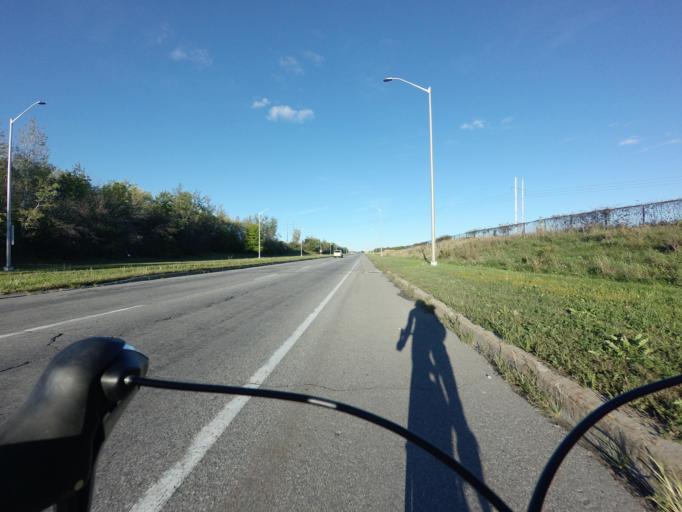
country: CA
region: Ontario
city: Bells Corners
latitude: 45.3187
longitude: -75.7854
